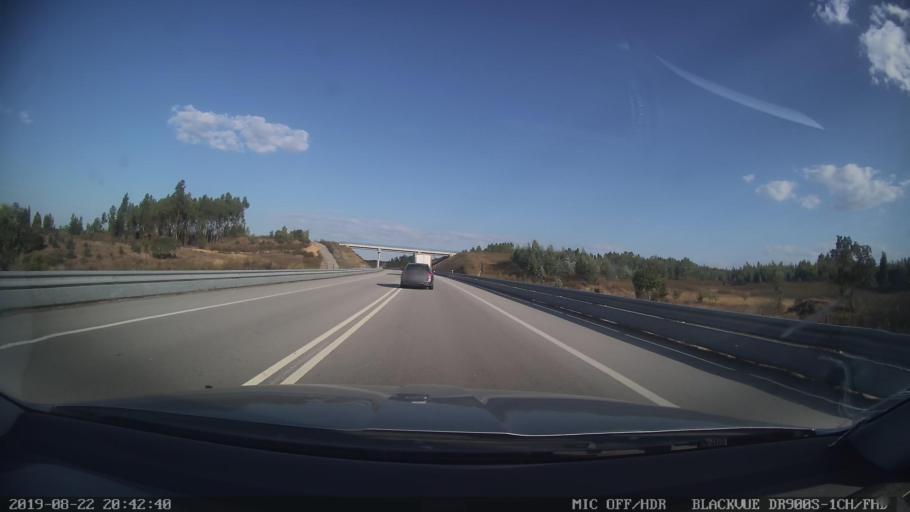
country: PT
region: Castelo Branco
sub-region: Proenca-A-Nova
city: Proenca-a-Nova
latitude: 39.6963
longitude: -7.8198
